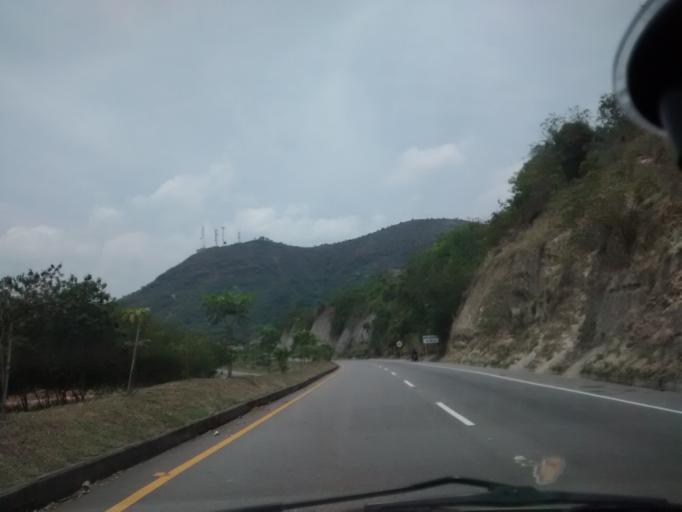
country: CO
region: Tolima
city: Espinal
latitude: 4.2181
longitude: -74.9650
